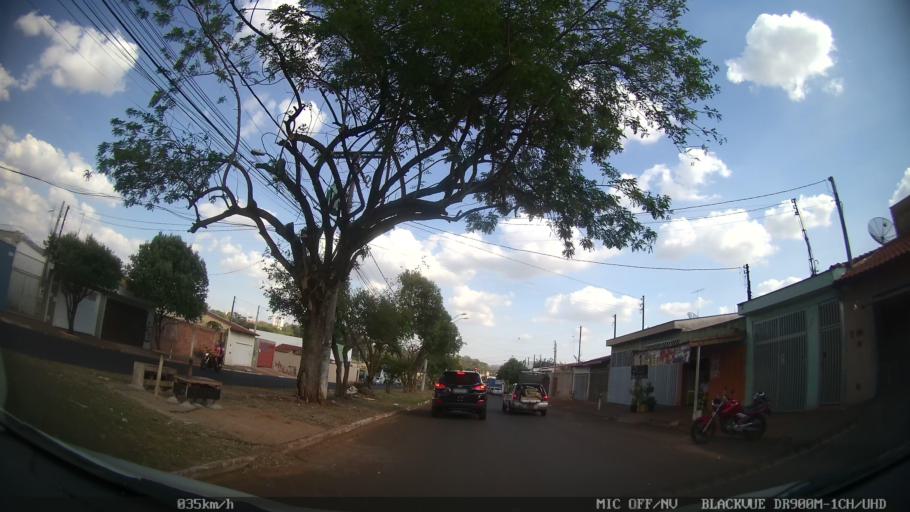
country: BR
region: Sao Paulo
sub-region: Ribeirao Preto
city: Ribeirao Preto
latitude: -21.2012
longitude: -47.8294
